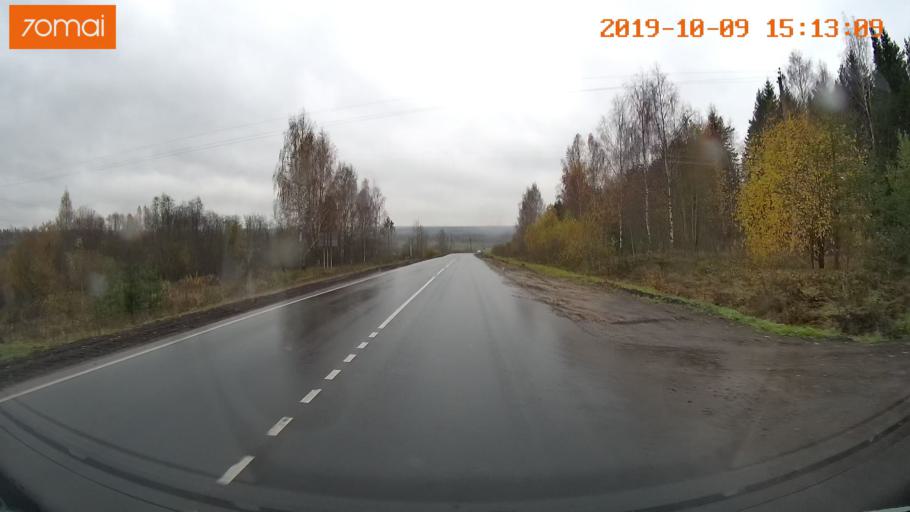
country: RU
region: Kostroma
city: Susanino
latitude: 58.1494
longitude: 41.6151
